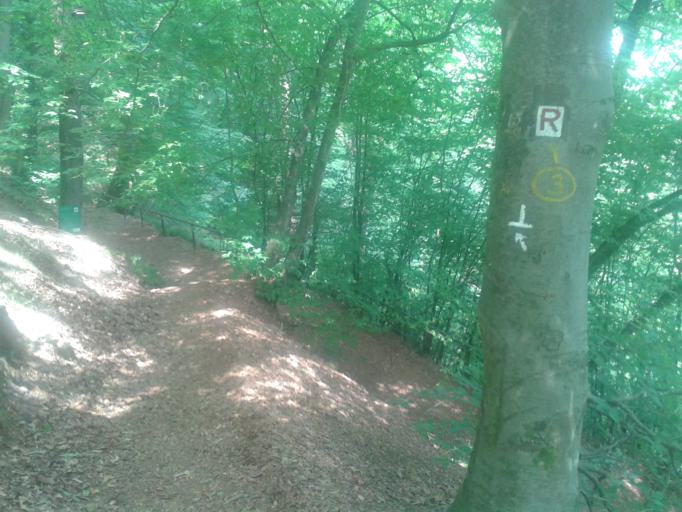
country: DE
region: Hesse
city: Neckarsteinach
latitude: 49.4075
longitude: 8.8243
